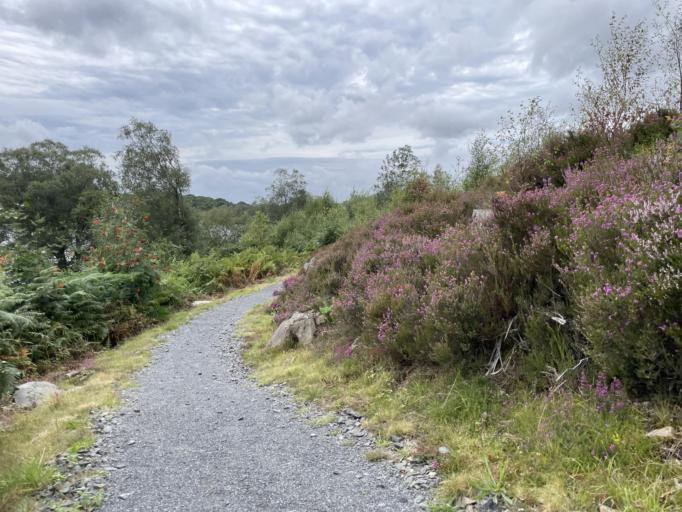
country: GB
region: Scotland
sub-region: Dumfries and Galloway
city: Newton Stewart
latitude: 55.0839
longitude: -4.5035
